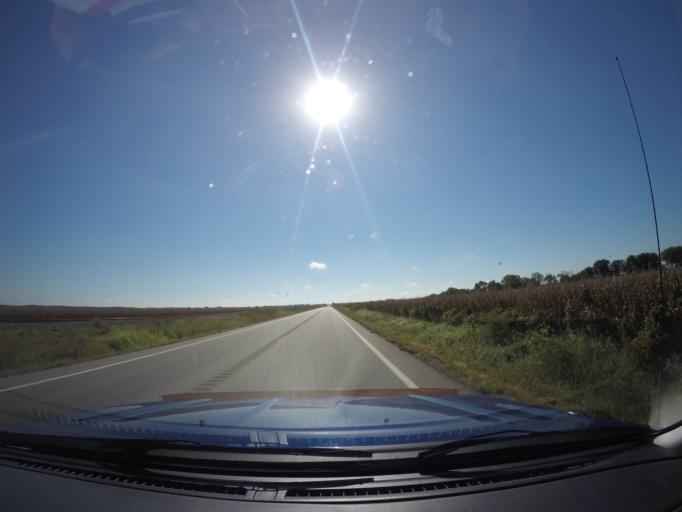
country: US
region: Kansas
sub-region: Shawnee County
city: Rossville
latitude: 39.1557
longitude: -95.9893
